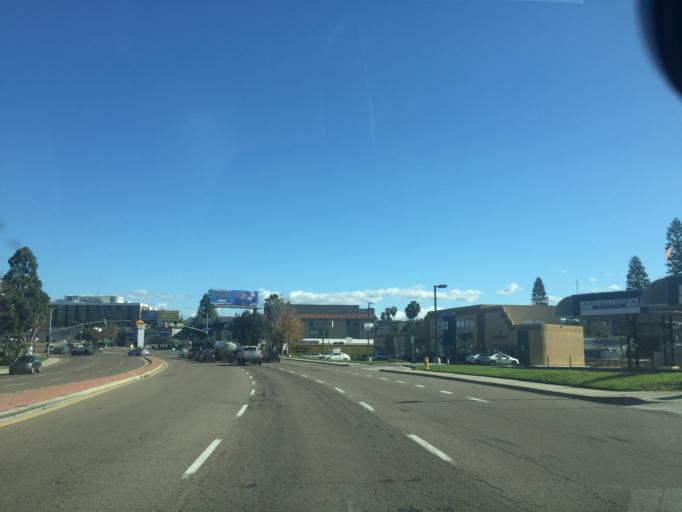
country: US
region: California
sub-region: San Diego County
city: La Mesa
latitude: 32.7903
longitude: -117.1010
